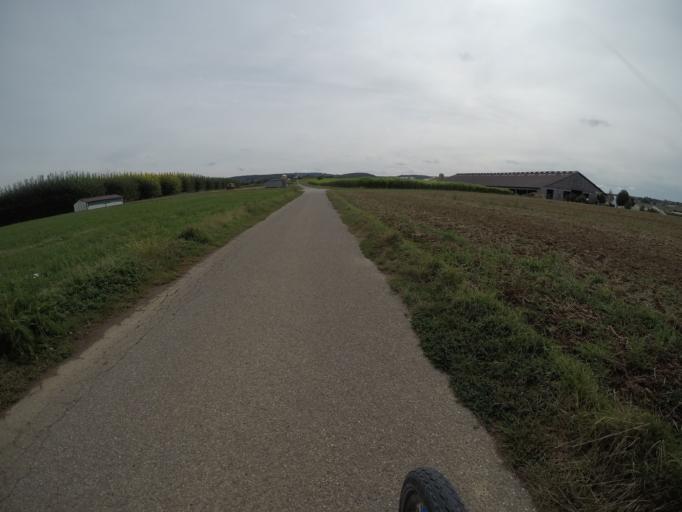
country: DE
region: Baden-Wuerttemberg
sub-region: Karlsruhe Region
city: Oberderdingen
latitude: 49.0779
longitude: 8.7959
